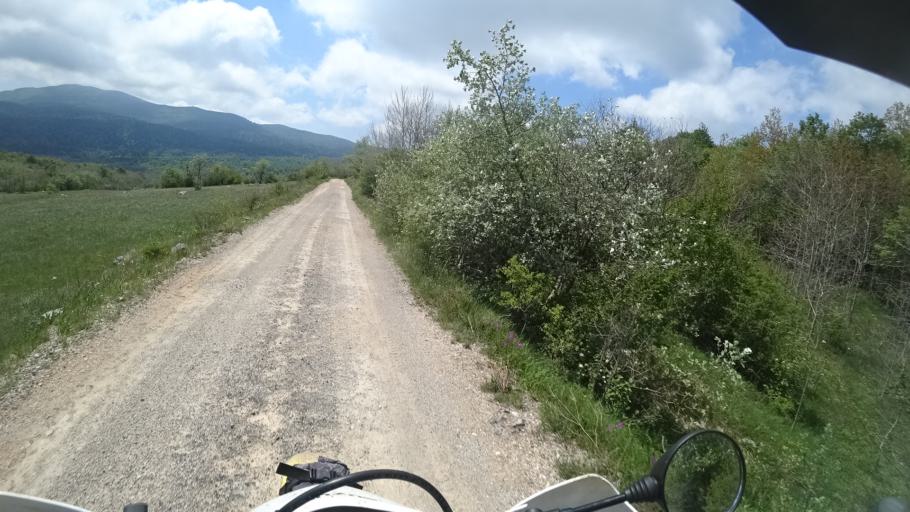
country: HR
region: Zadarska
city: Gracac
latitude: 44.5066
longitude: 15.8859
